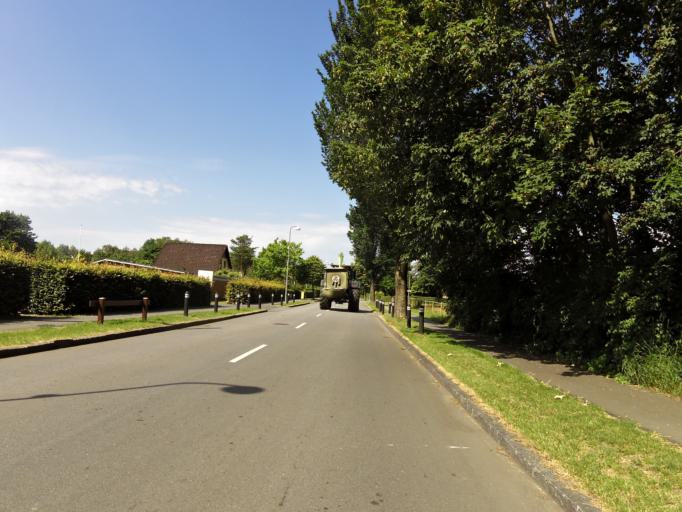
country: DK
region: South Denmark
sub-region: Haderslev Kommune
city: Vojens
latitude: 55.1991
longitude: 9.2033
